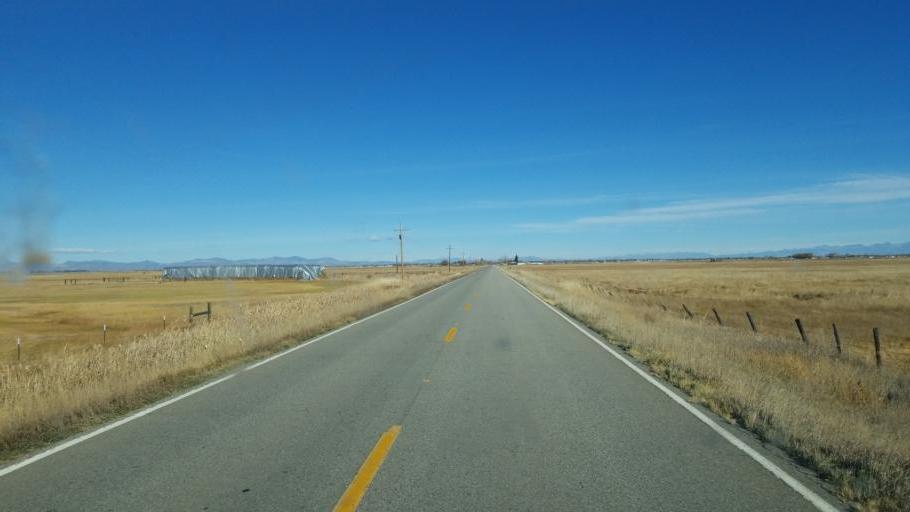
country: US
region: Colorado
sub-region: Rio Grande County
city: Monte Vista
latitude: 37.5287
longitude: -106.1493
